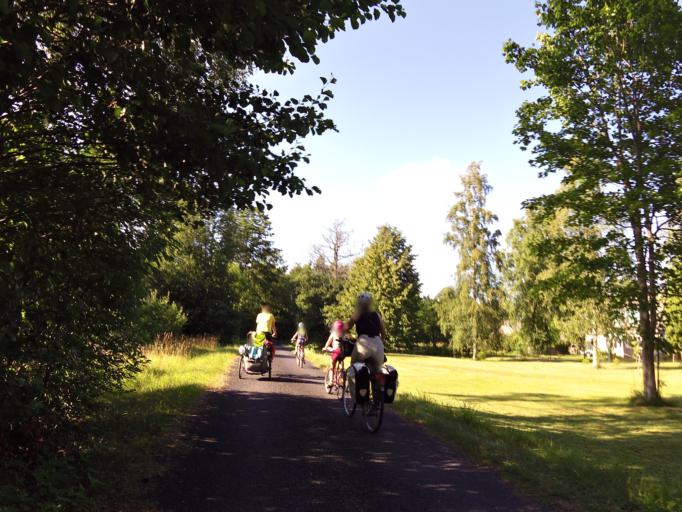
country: EE
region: Hiiumaa
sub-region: Kaerdla linn
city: Kardla
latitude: 58.7758
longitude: 22.4843
